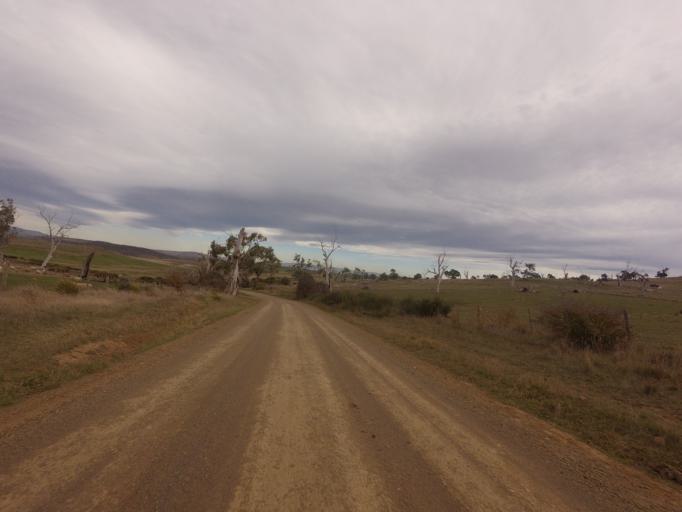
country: AU
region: Tasmania
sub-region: Derwent Valley
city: New Norfolk
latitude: -42.3885
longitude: 146.9783
